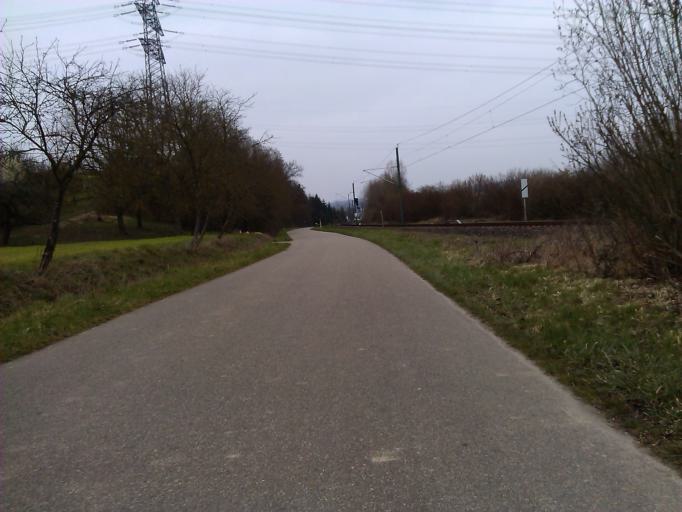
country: DE
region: Baden-Wuerttemberg
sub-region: Karlsruhe Region
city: Zuzenhausen
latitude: 49.3075
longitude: 8.8141
